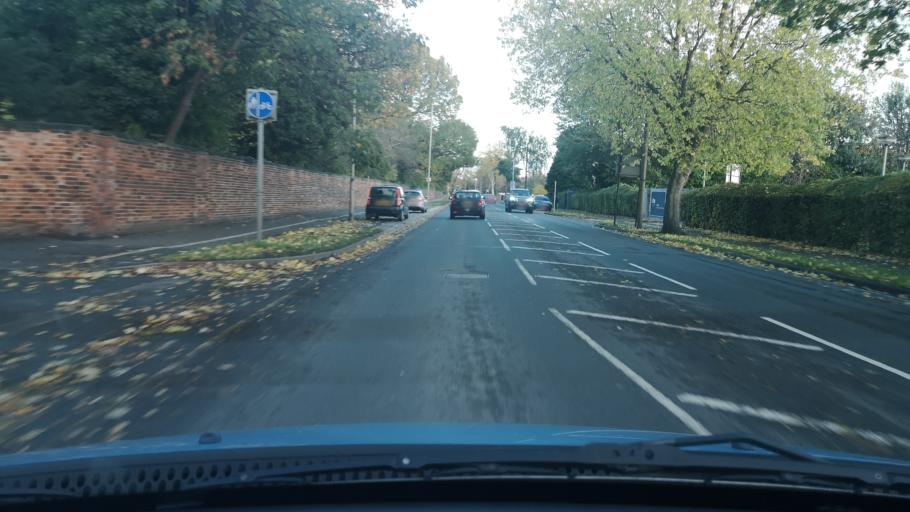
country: GB
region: England
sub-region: City and Borough of Wakefield
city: Wakefield
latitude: 53.6709
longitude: -1.5155
